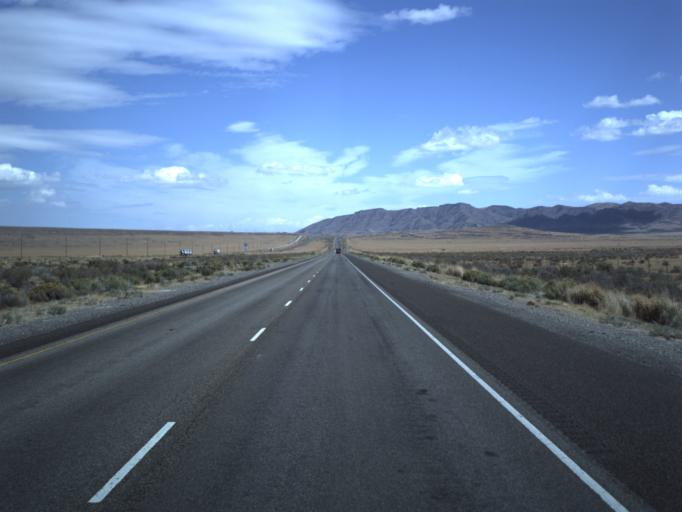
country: US
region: Utah
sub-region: Tooele County
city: Grantsville
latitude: 40.7471
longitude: -113.0570
